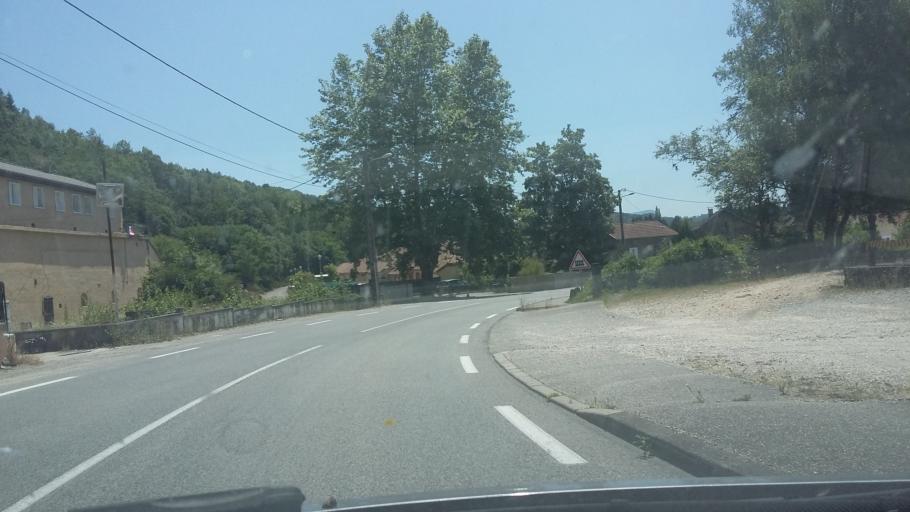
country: FR
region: Rhone-Alpes
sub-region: Departement de l'Ain
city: Belley
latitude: 45.8061
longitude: 5.6830
